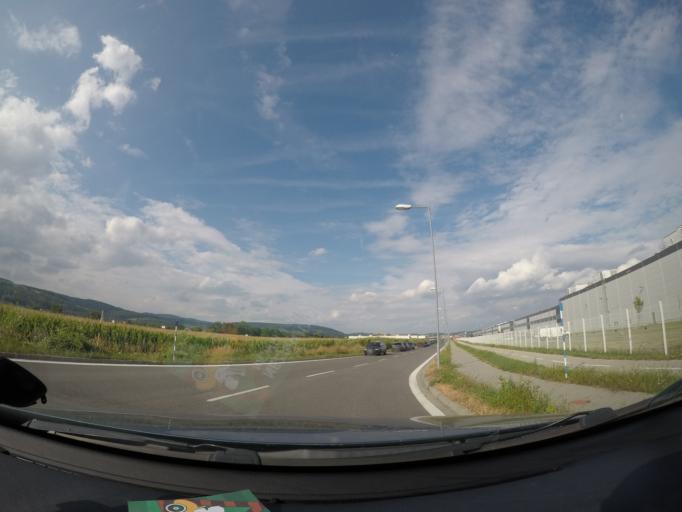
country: SK
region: Trenciansky
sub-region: Okres Trencin
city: Trencin
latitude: 48.8854
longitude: 17.9904
